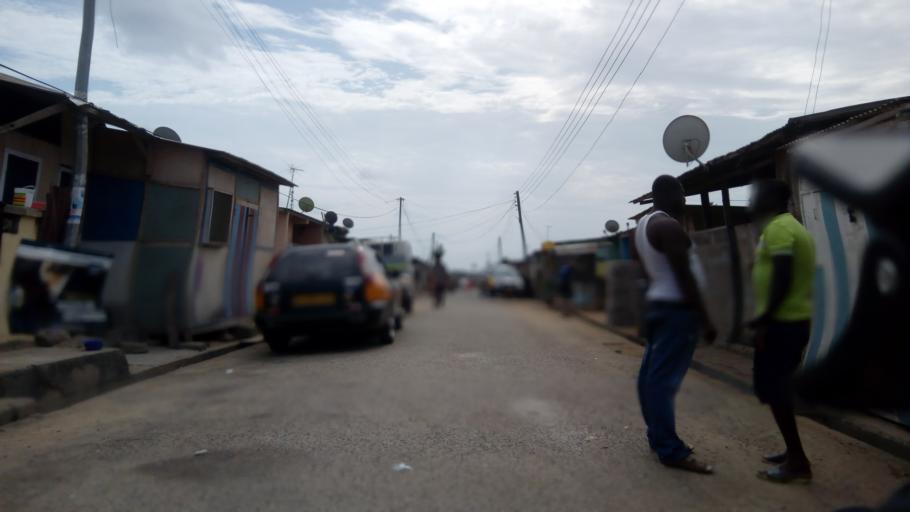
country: GH
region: Central
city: Cape Coast
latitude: 5.1016
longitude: -1.2770
